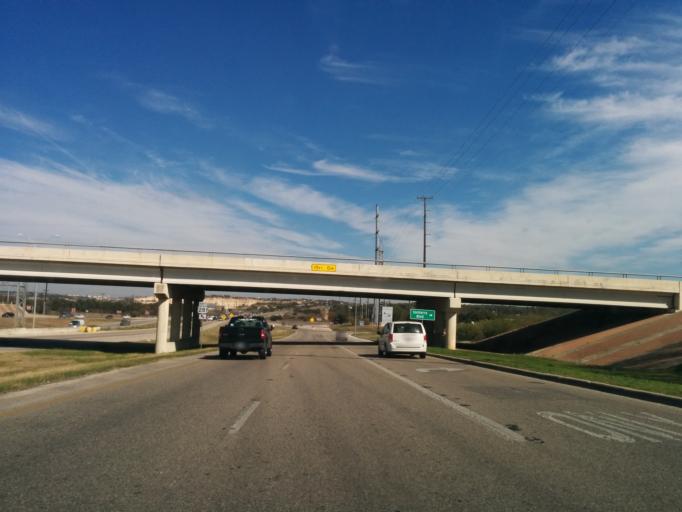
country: US
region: Texas
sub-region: Bexar County
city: Hollywood Park
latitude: 29.6137
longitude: -98.4666
